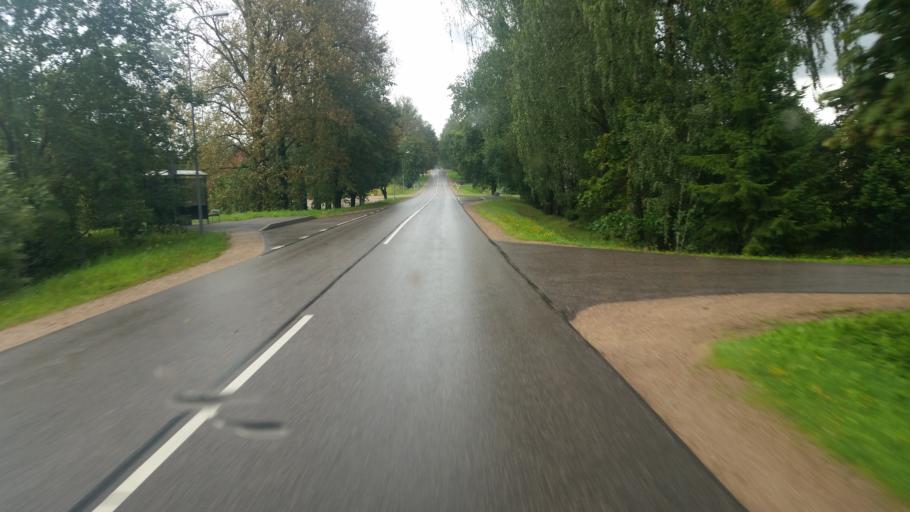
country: LV
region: Bauskas Rajons
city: Bauska
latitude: 56.4321
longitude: 24.3373
